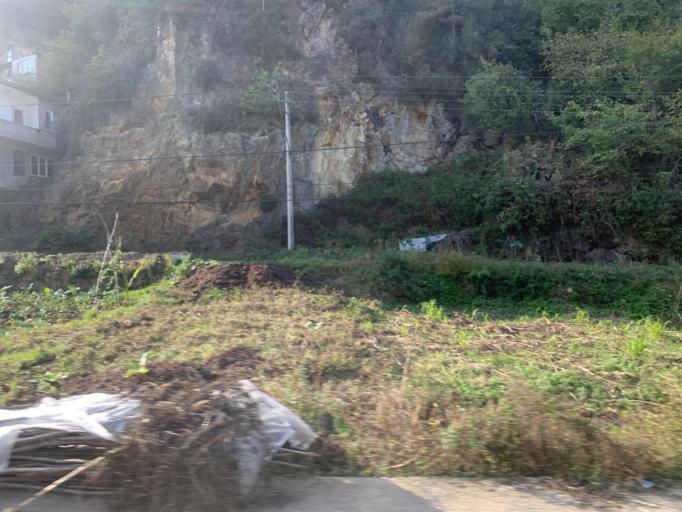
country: TR
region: Trabzon
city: Dernekpazari
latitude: 40.8290
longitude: 40.2686
